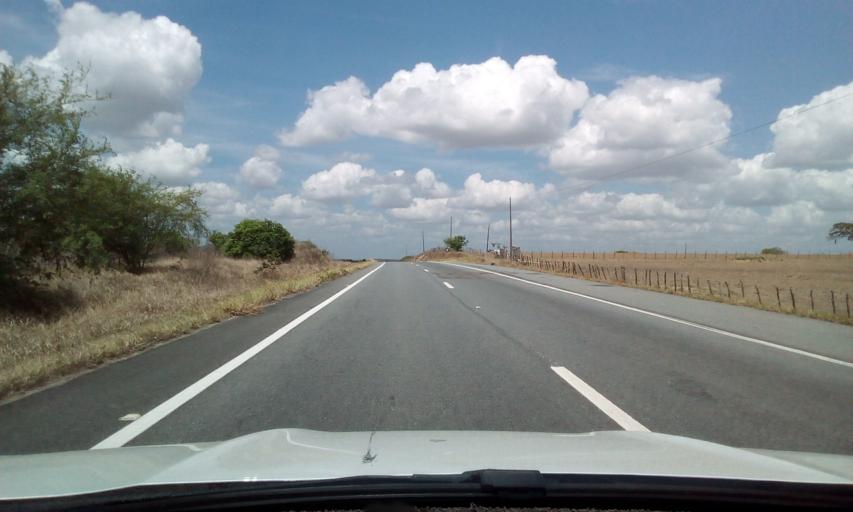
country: BR
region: Paraiba
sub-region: Pilar
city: Pilar
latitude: -7.1763
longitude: -35.3248
